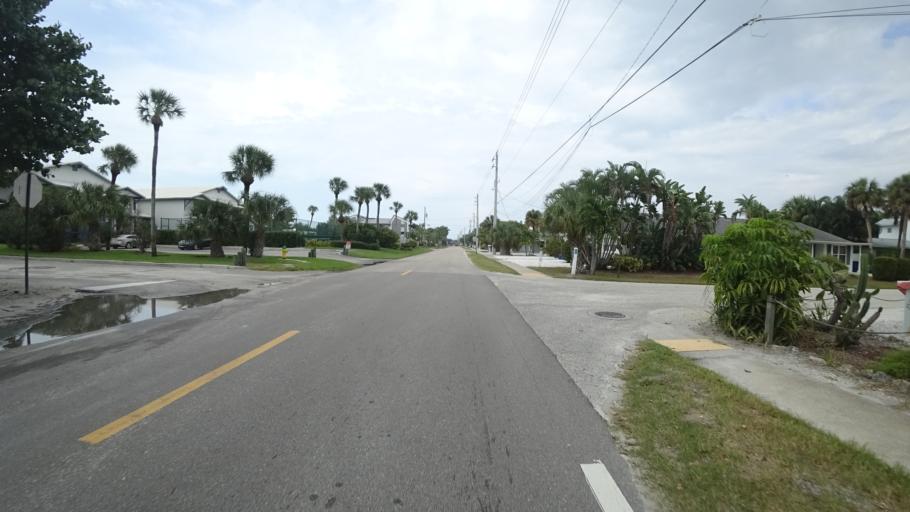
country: US
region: Florida
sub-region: Manatee County
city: Holmes Beach
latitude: 27.5126
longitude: -82.7218
